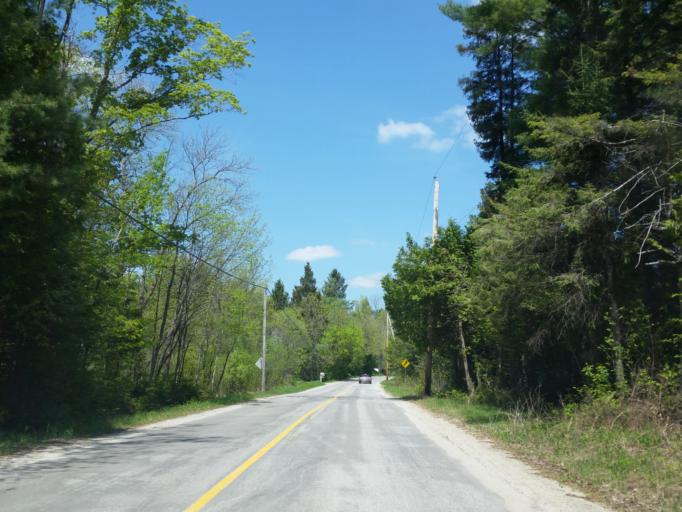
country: CA
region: Quebec
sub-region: Outaouais
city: Wakefield
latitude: 45.6263
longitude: -75.9066
